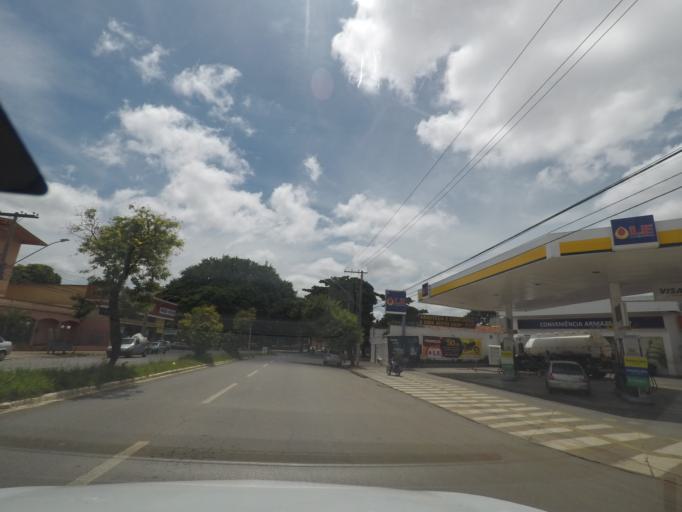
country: BR
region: Goias
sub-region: Goiania
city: Goiania
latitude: -16.6598
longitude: -49.2457
